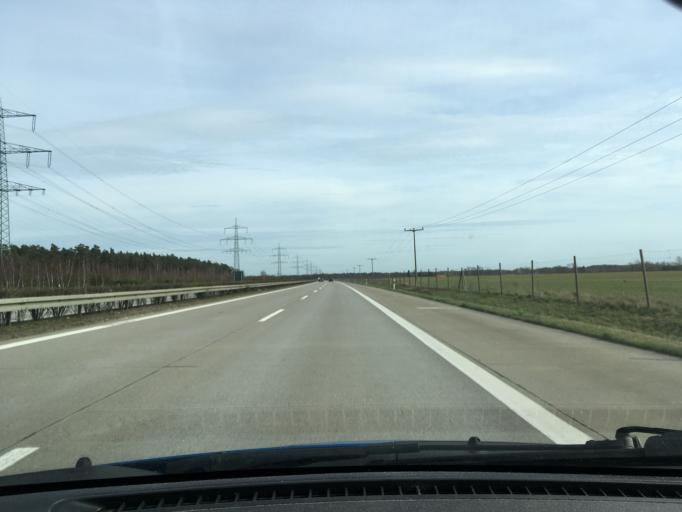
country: DE
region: Mecklenburg-Vorpommern
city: Zarrentin
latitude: 53.5110
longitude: 10.9146
